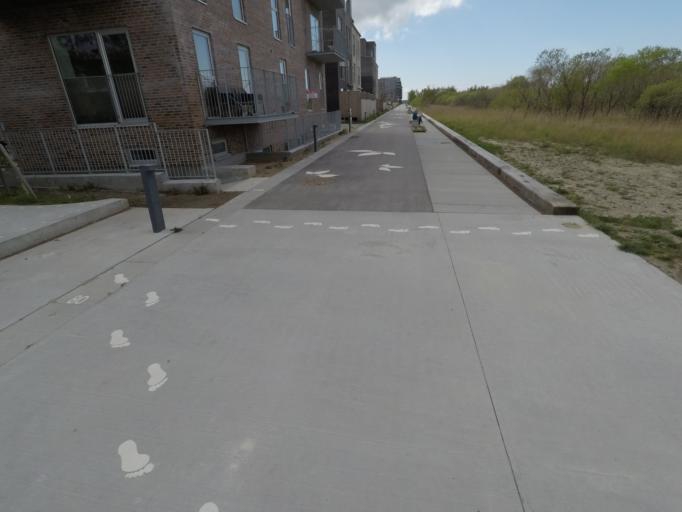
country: DK
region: Capital Region
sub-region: Tarnby Kommune
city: Tarnby
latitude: 55.6238
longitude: 12.5687
